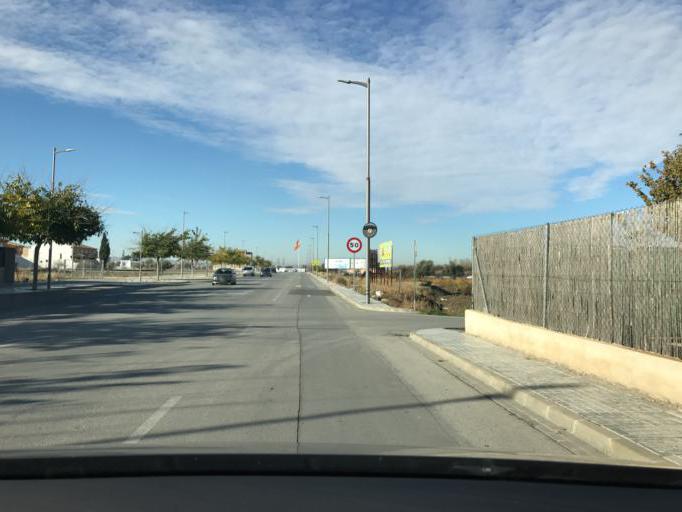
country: ES
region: Andalusia
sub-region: Provincia de Granada
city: Churriana de la Vega
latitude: 37.1510
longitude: -3.6488
